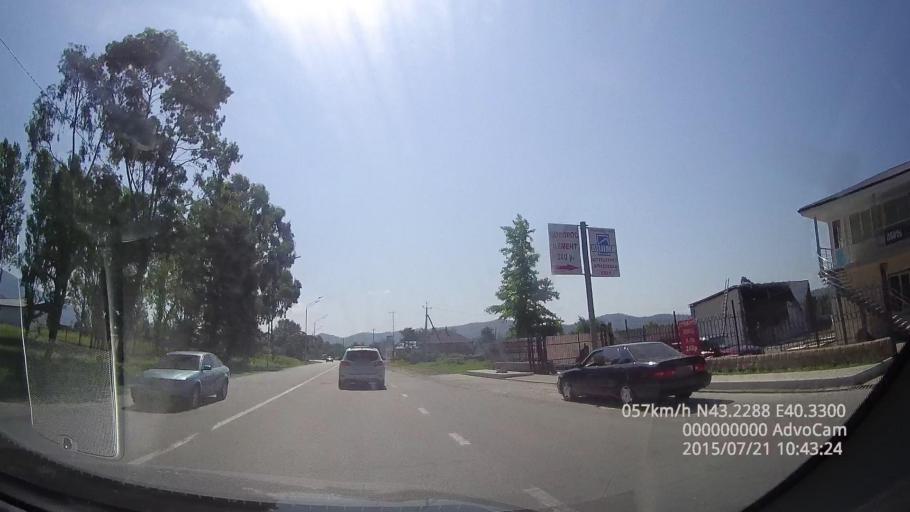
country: GE
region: Abkhazia
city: Bich'vinta
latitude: 43.2288
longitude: 40.3302
